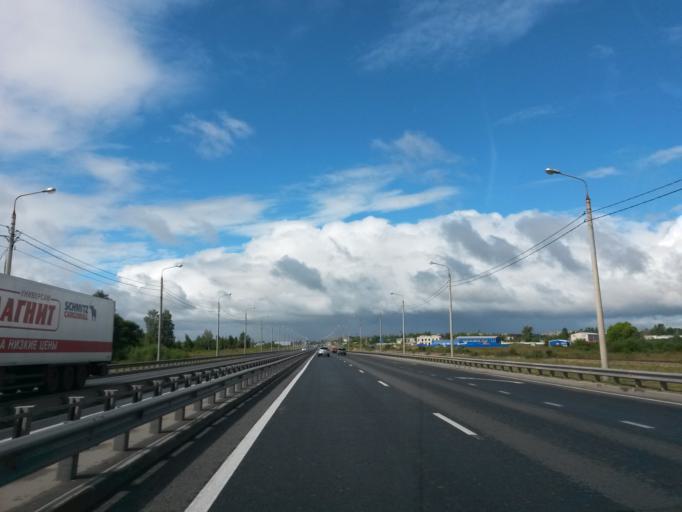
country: RU
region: Jaroslavl
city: Yaroslavl
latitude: 57.6682
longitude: 39.8102
